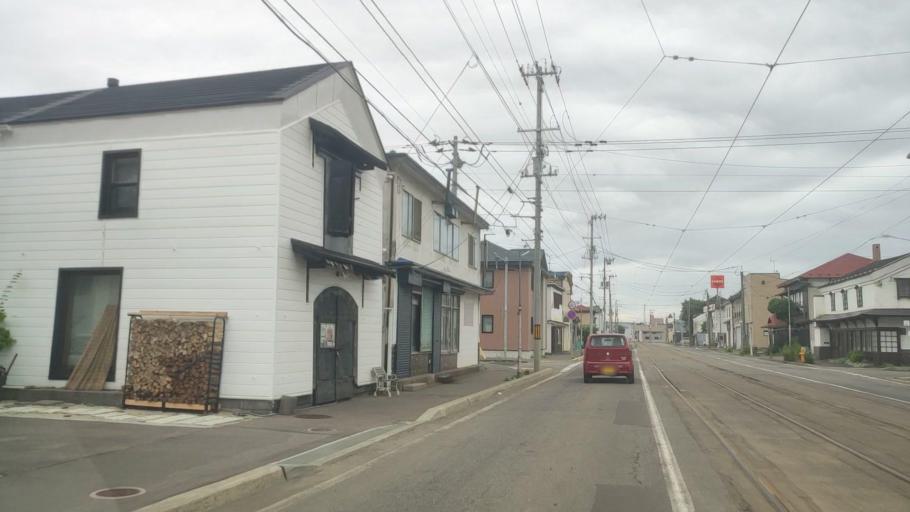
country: JP
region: Hokkaido
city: Hakodate
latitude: 41.7714
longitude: 140.7072
